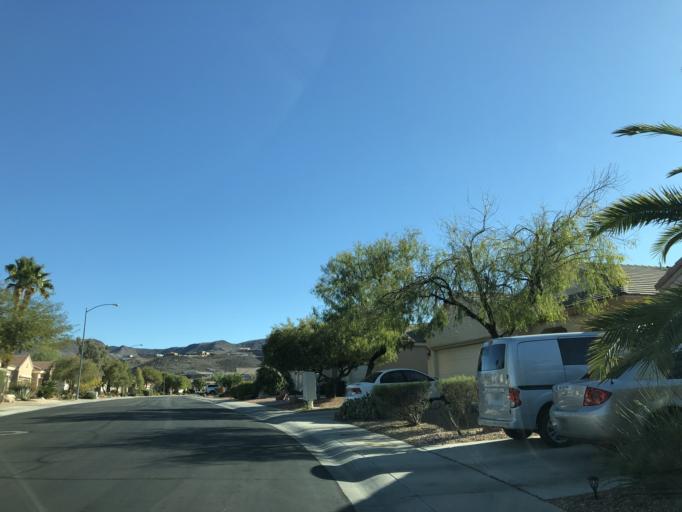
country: US
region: Nevada
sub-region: Clark County
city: Whitney
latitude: 36.0052
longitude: -115.0700
